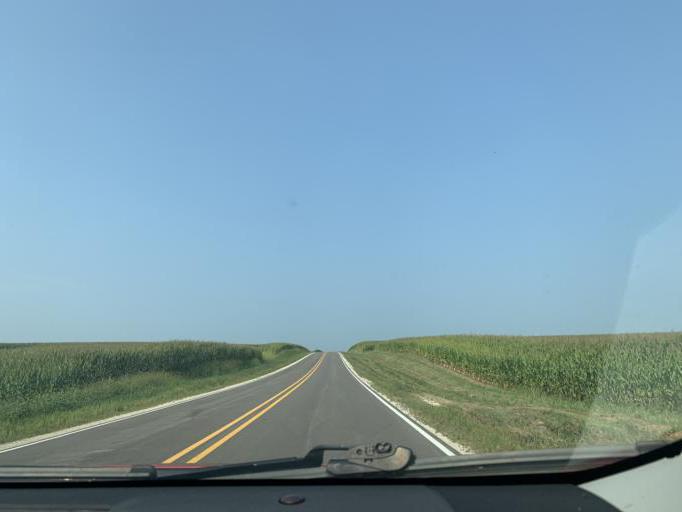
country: US
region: Illinois
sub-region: Whiteside County
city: Sterling
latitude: 41.8441
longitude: -89.7687
